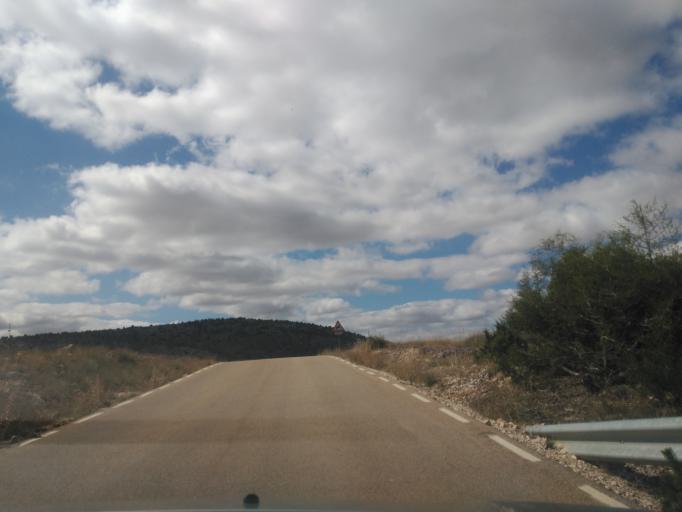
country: ES
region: Castille and Leon
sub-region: Provincia de Soria
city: Espejon
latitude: 41.8337
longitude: -3.2484
